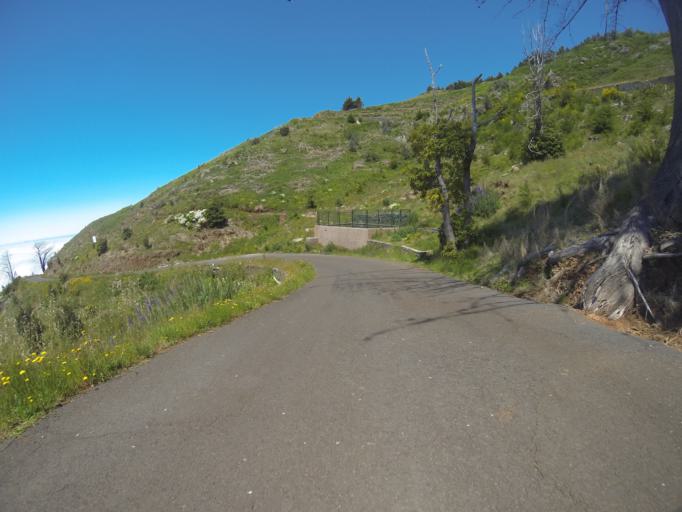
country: PT
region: Madeira
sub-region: Funchal
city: Nossa Senhora do Monte
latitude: 32.7044
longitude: -16.9119
